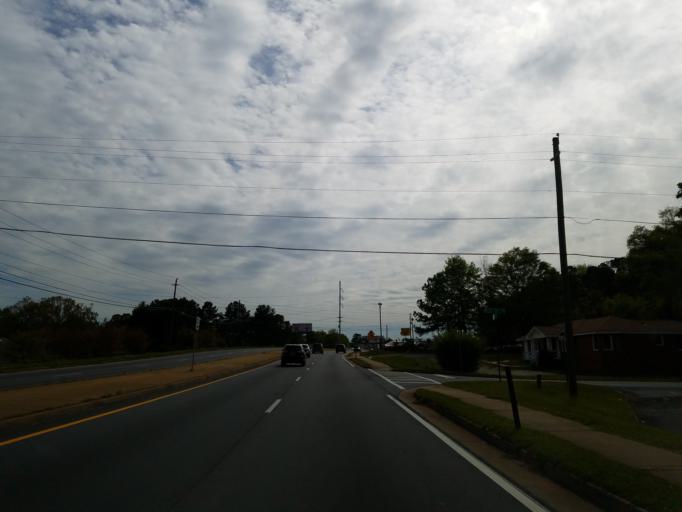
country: US
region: Georgia
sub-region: Cobb County
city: Fair Oaks
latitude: 33.9002
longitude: -84.5709
